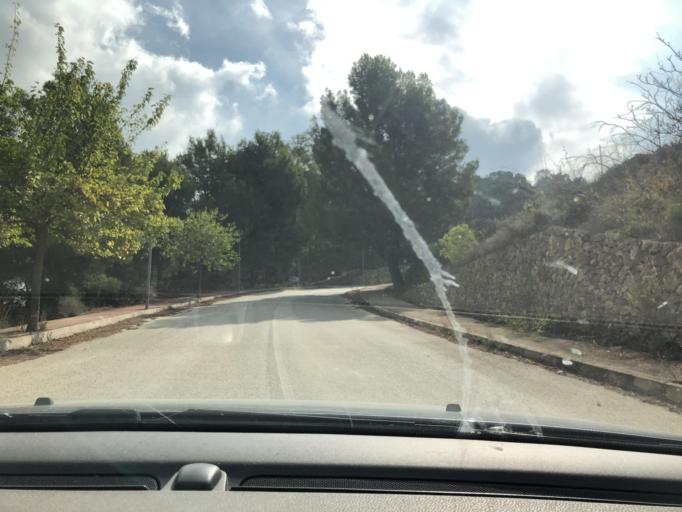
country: ES
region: Valencia
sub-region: Provincia de Alicante
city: Callosa d'En Sarria
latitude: 38.6360
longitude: -0.1124
